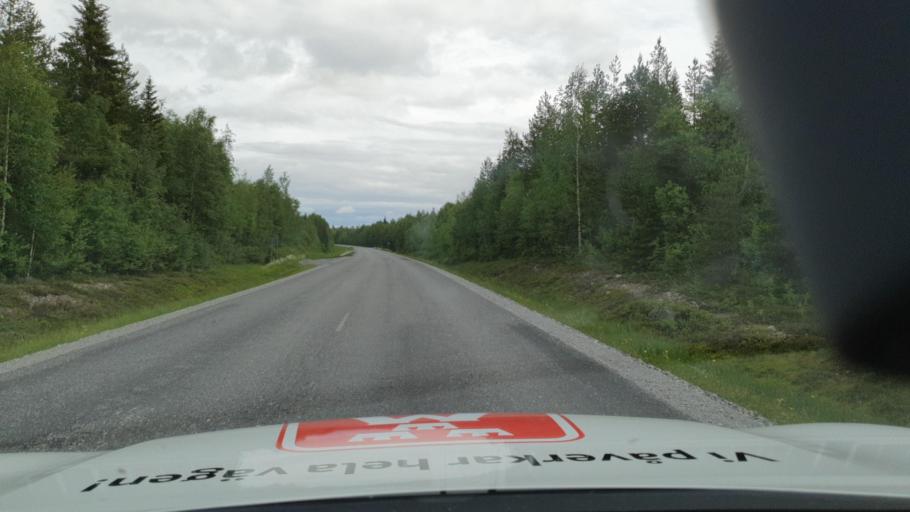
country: SE
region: Vaesterbotten
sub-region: Dorotea Kommun
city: Dorotea
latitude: 64.2303
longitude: 16.8144
